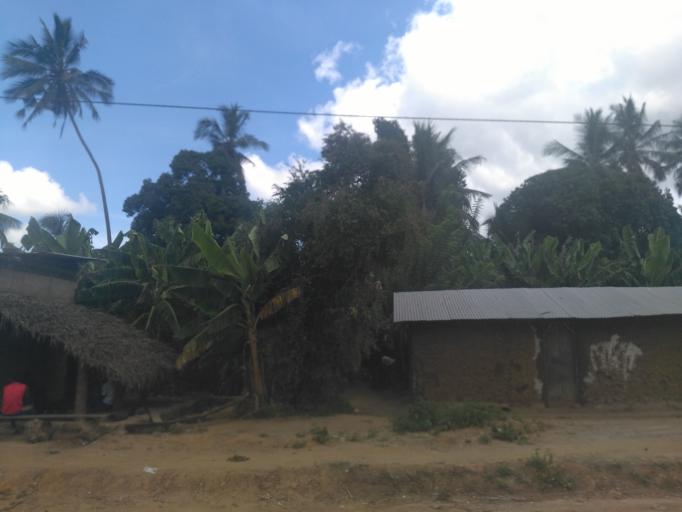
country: TZ
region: Zanzibar North
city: Gamba
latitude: -5.9732
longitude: 39.3025
